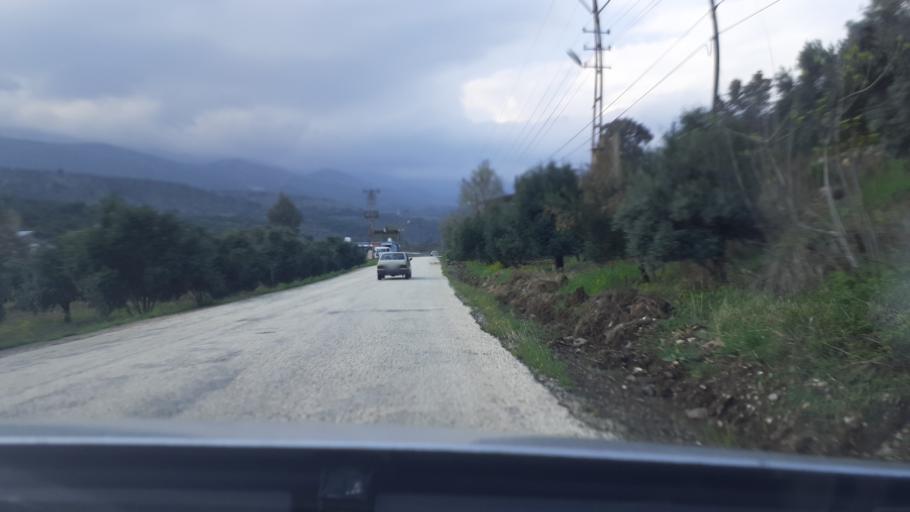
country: TR
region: Hatay
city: Kirikhan
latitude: 36.5049
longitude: 36.3234
